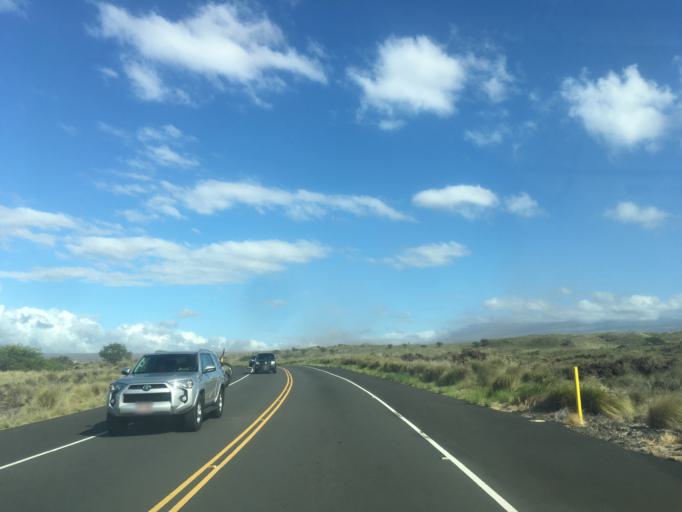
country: US
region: Hawaii
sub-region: Hawaii County
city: Waikoloa Village
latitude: 19.9093
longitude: -155.8155
